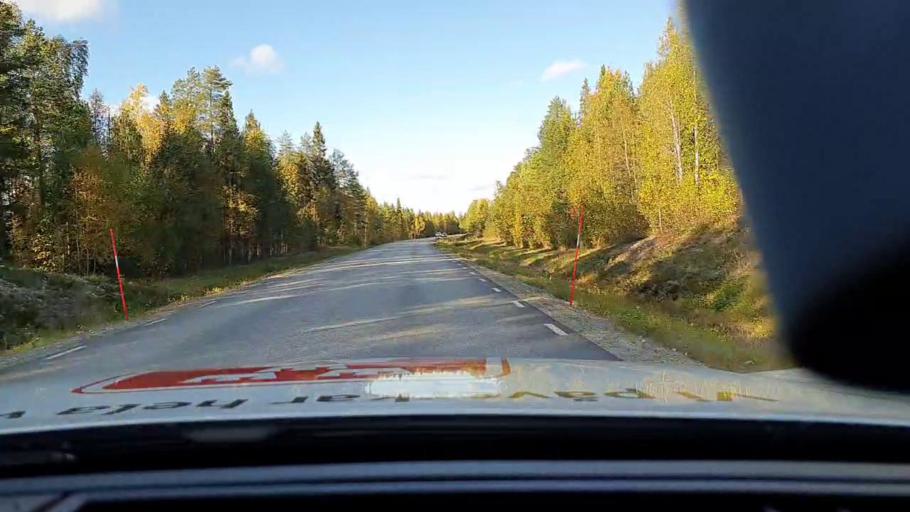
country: SE
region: Norrbotten
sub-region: Pitea Kommun
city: Norrfjarden
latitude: 65.4985
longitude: 21.4756
